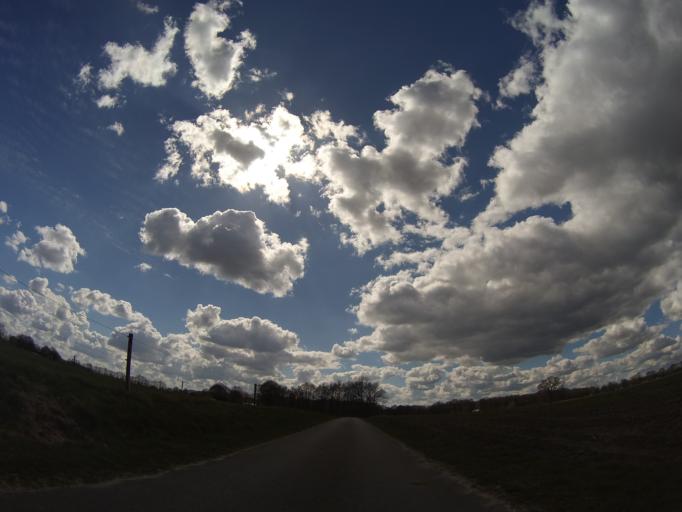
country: NL
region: Drenthe
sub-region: Gemeente Coevorden
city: Sleen
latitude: 52.7719
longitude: 6.8148
